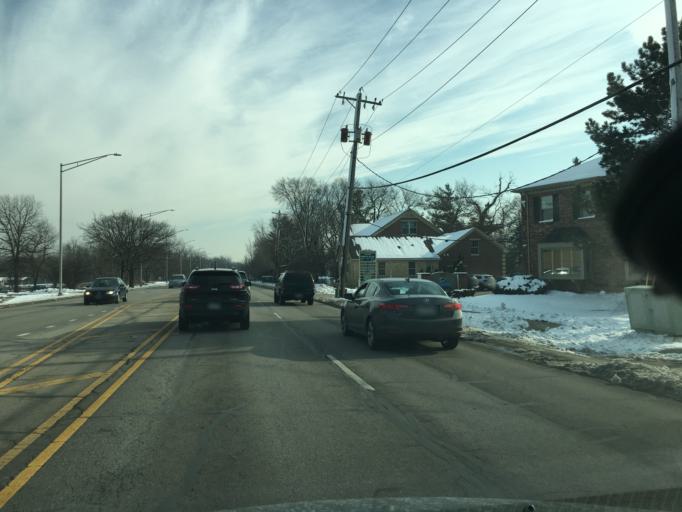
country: US
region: Illinois
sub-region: DuPage County
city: Naperville
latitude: 41.7548
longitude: -88.1389
